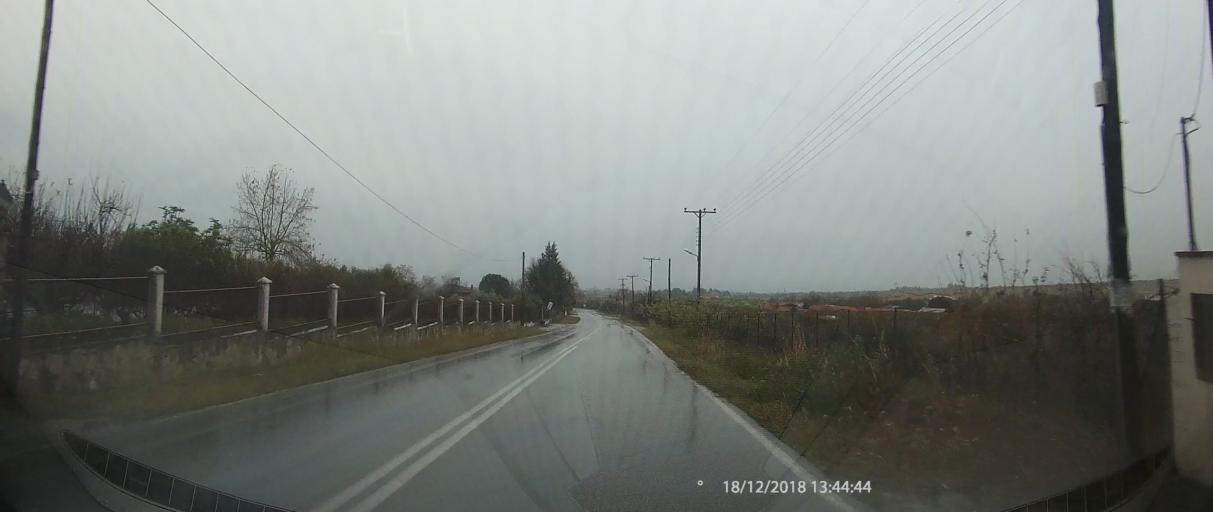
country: GR
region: Central Macedonia
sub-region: Nomos Pierias
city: Litochoro
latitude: 40.1008
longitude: 22.5341
